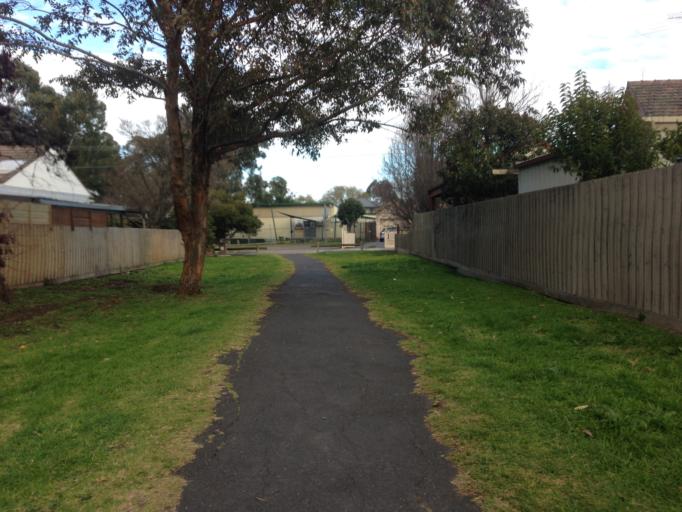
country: AU
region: Victoria
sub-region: Banyule
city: Bellfield
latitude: -37.7636
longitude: 145.0386
